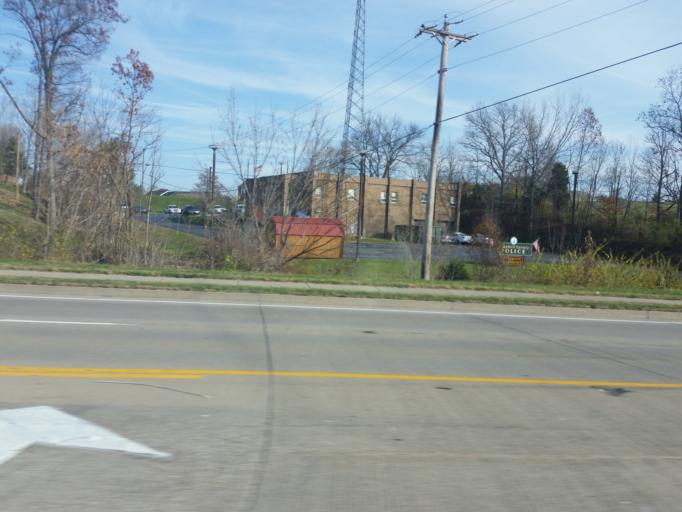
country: US
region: Kentucky
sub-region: Campbell County
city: Alexandria
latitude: 38.9501
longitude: -84.3936
